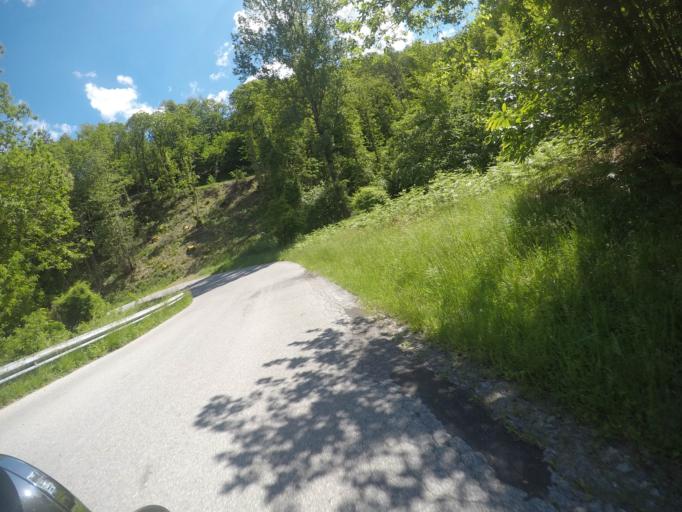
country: IT
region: Tuscany
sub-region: Provincia di Lucca
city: Careggine
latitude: 44.1325
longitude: 10.3350
